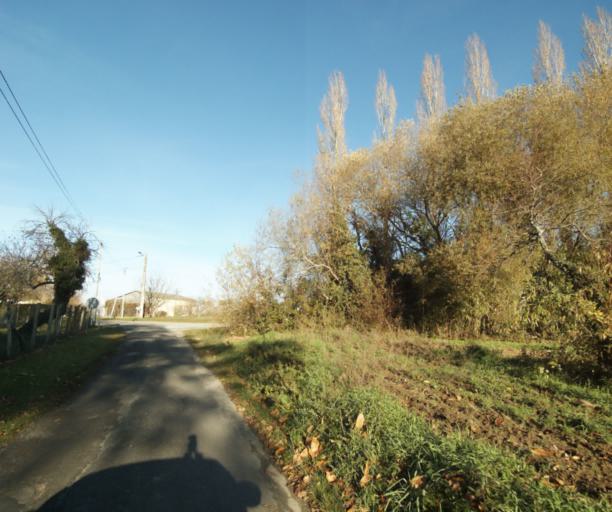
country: FR
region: Poitou-Charentes
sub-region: Departement de la Charente-Maritime
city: Cherac
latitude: 45.7299
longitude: -0.4753
